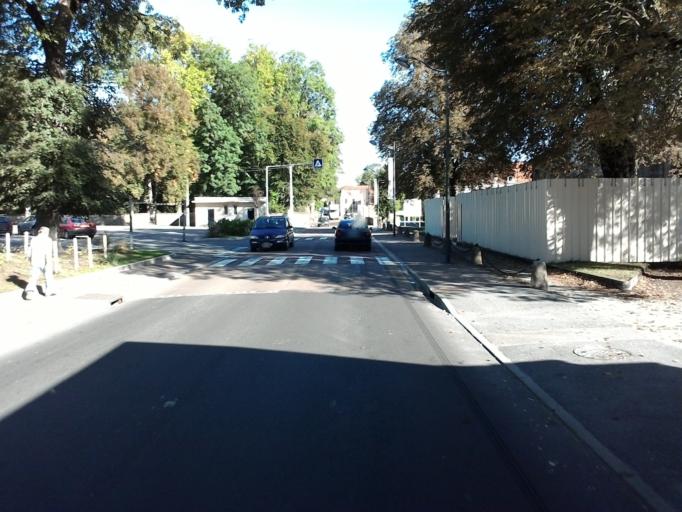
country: FR
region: Bourgogne
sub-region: Departement de la Cote-d'Or
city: Chatillon-sur-Seine
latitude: 47.8630
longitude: 4.5747
